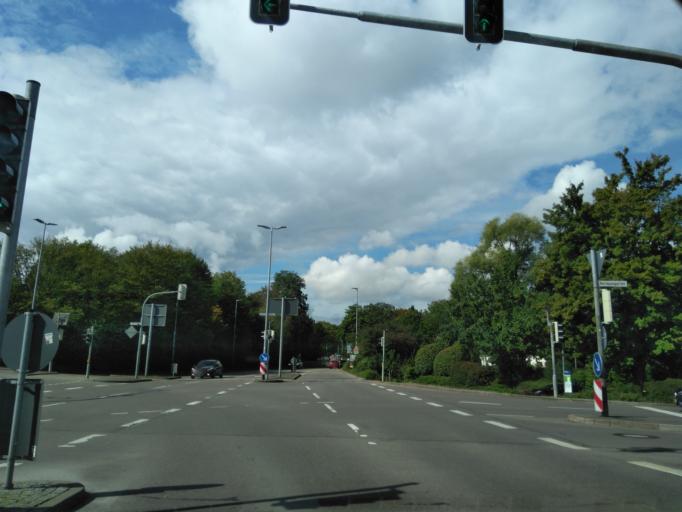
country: DE
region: Baden-Wuerttemberg
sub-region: Regierungsbezirk Stuttgart
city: Bietigheim-Bissingen
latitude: 48.9582
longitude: 9.1272
